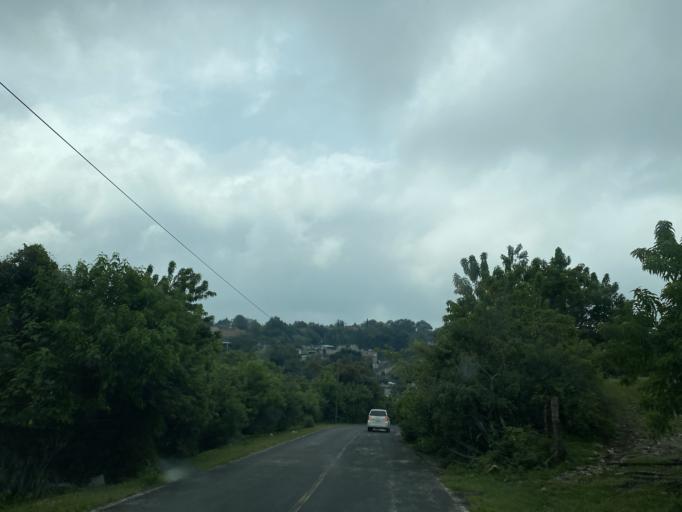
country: MX
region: Morelos
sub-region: Yecapixtla
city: Achichipico
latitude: 18.9541
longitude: -98.8262
